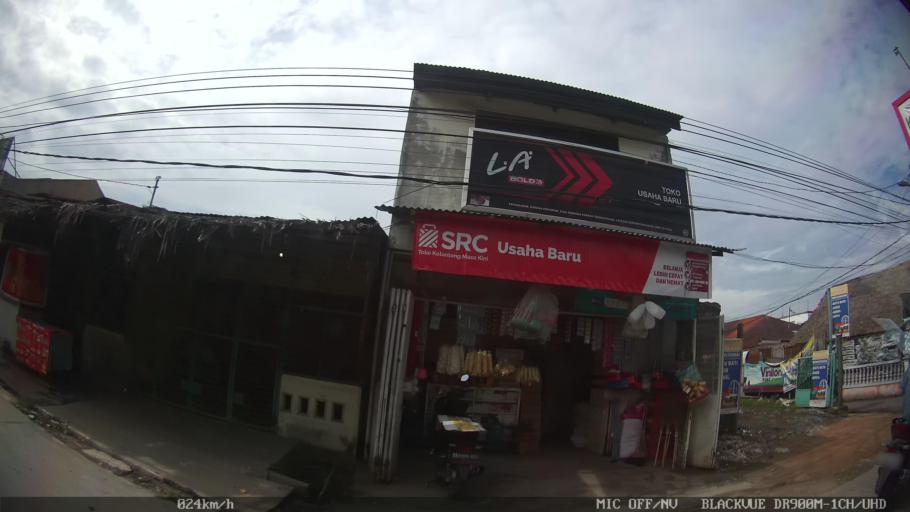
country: ID
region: North Sumatra
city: Sunggal
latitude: 3.6059
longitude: 98.6181
